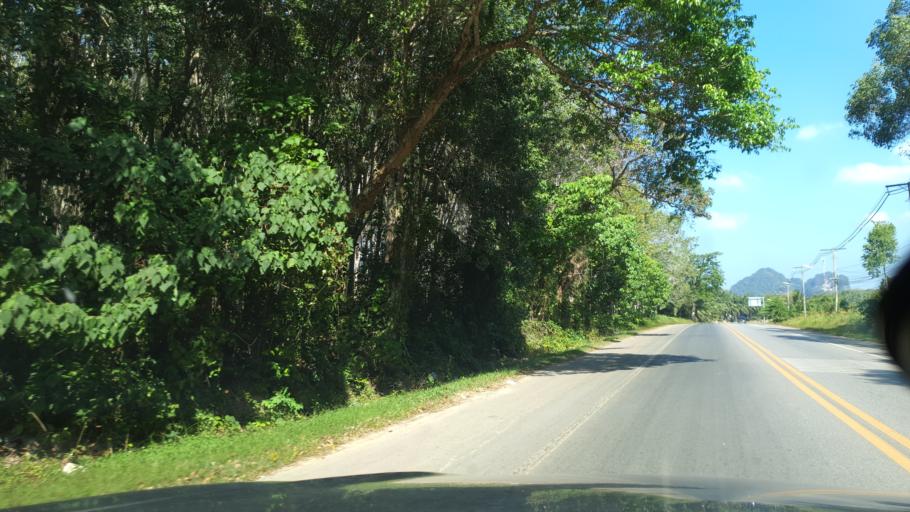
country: TH
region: Krabi
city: Krabi
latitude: 8.0653
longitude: 98.8592
